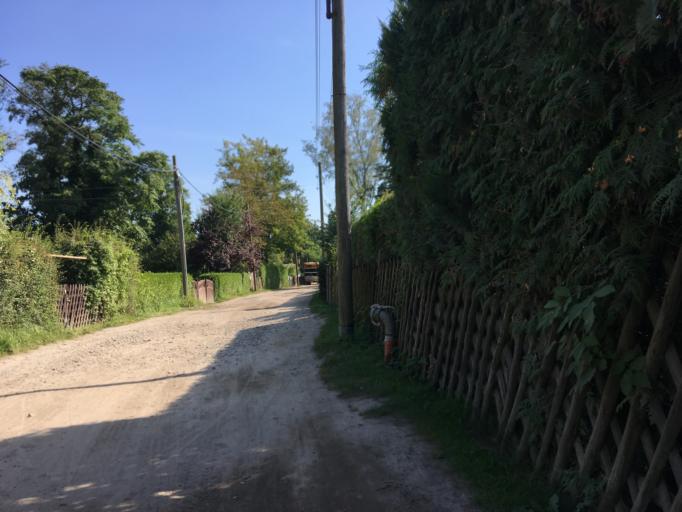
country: DE
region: Berlin
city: Rahnsdorf
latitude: 52.4313
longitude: 13.7089
